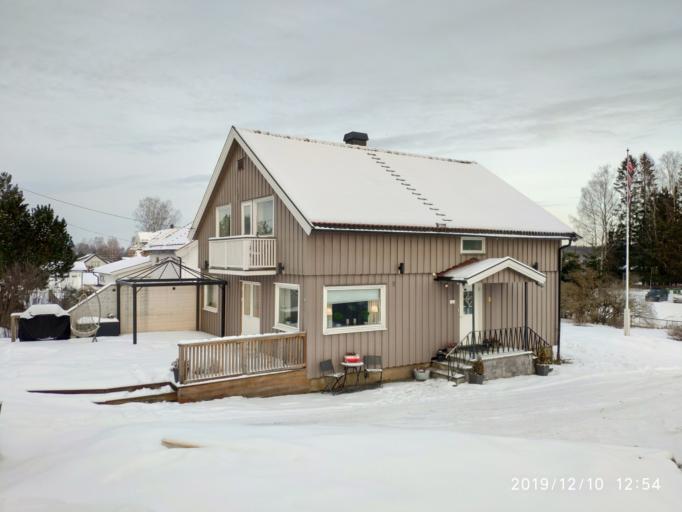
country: NO
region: Akershus
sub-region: Eidsvoll
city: Raholt
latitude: 60.2508
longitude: 11.2003
